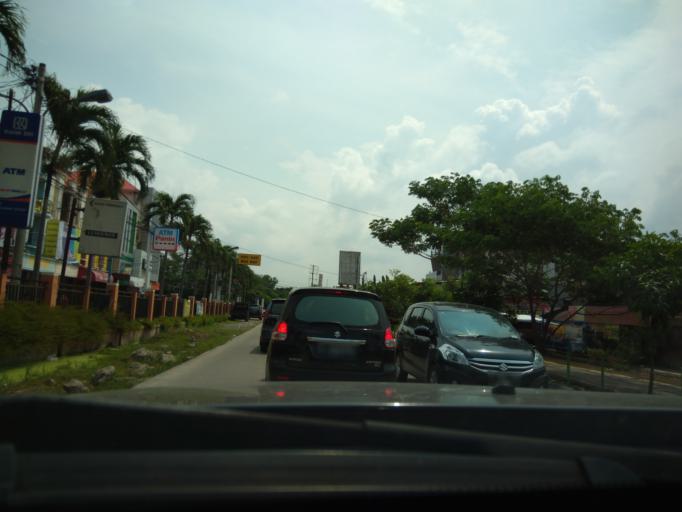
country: ID
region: West Java
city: Bekasi
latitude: -6.1832
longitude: 106.9783
